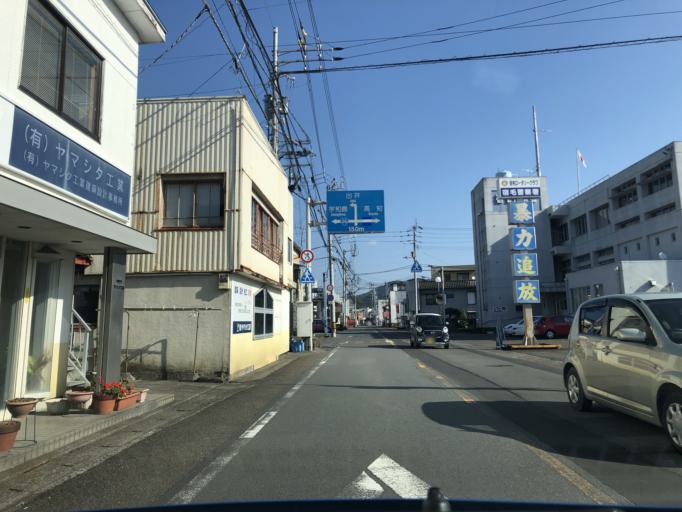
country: JP
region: Kochi
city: Sukumo
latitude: 32.9353
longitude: 132.7224
